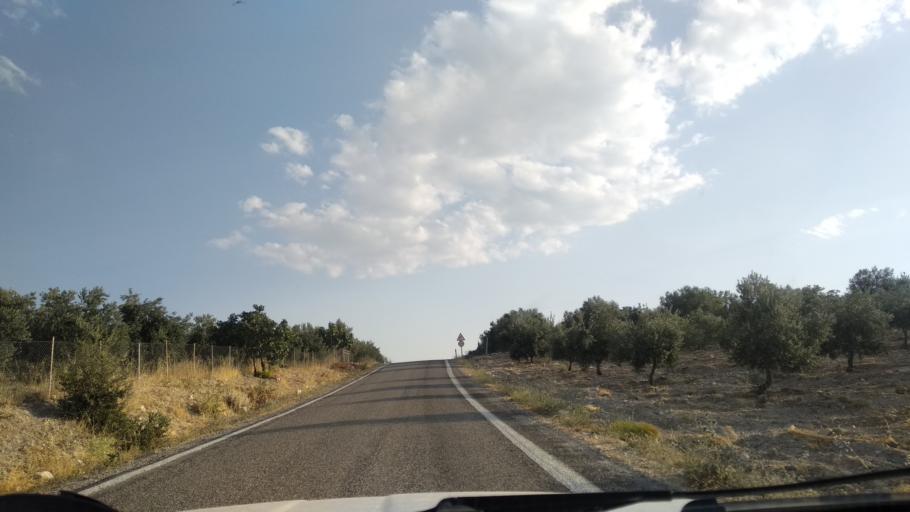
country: TR
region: Mersin
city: Sarikavak
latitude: 36.5657
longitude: 33.6337
